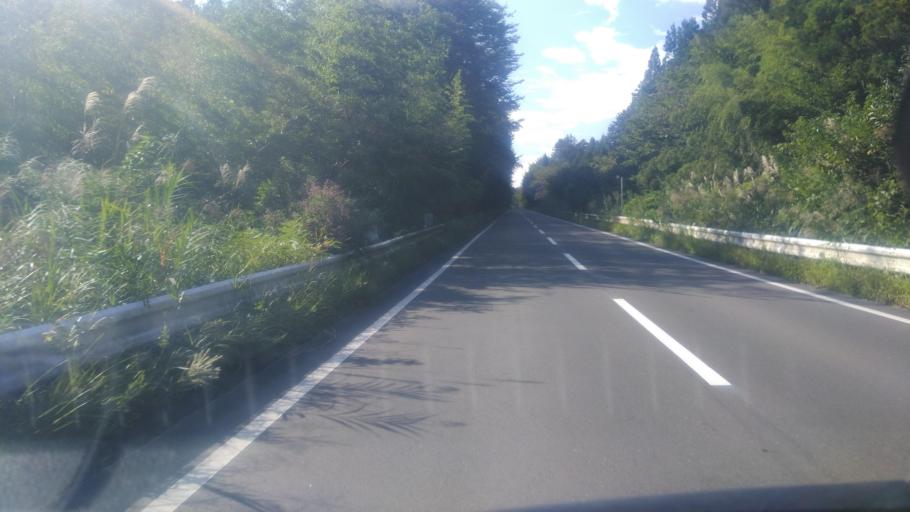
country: JP
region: Miyagi
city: Okawara
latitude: 38.0892
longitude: 140.7155
